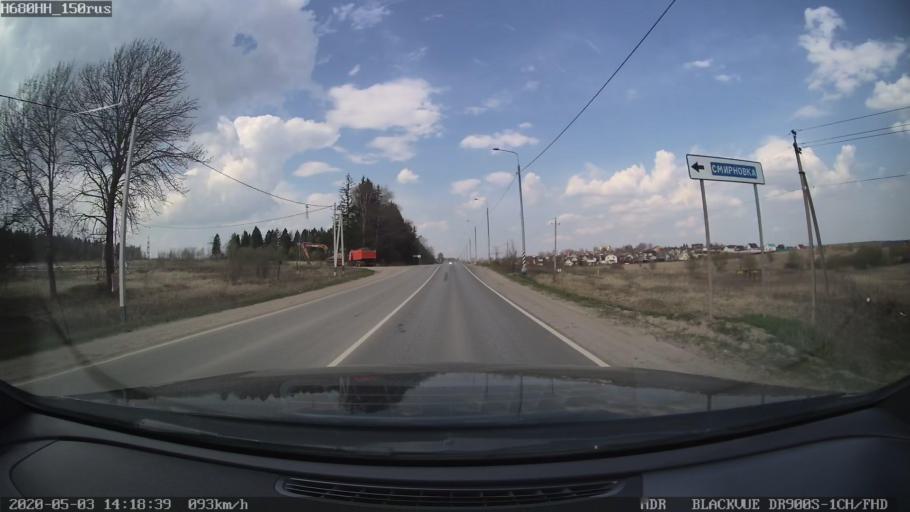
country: RU
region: Moskovskaya
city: Solnechnogorsk
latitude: 56.2218
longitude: 36.9710
